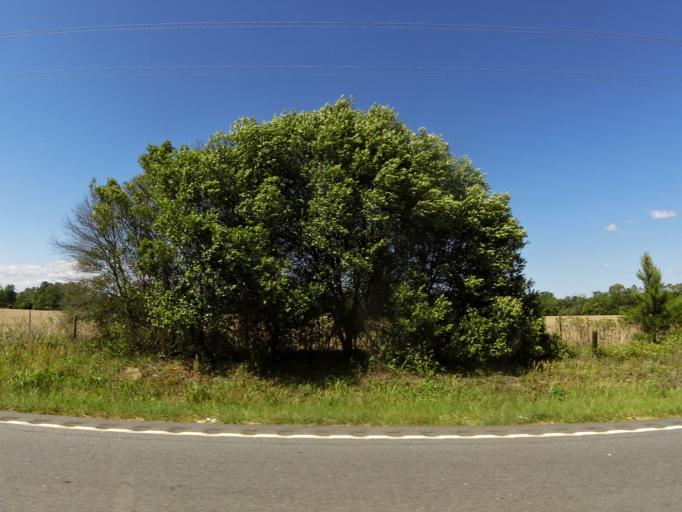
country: US
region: South Carolina
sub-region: Aiken County
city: Aiken
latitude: 33.5223
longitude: -81.6118
